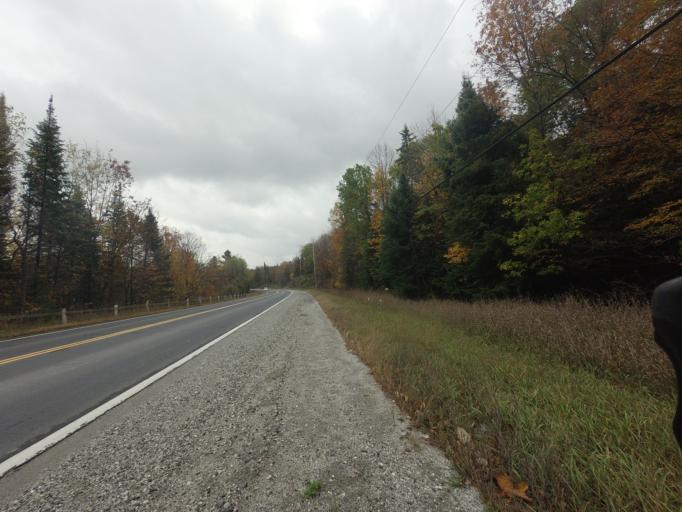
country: CA
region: Ontario
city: Perth
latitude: 45.1170
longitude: -76.4916
